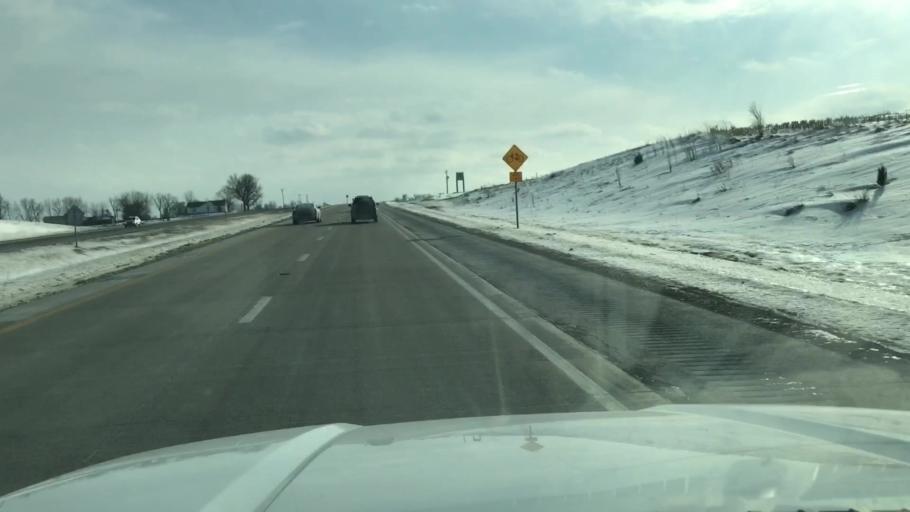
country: US
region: Missouri
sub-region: Nodaway County
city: Maryville
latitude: 40.3035
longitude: -94.8751
